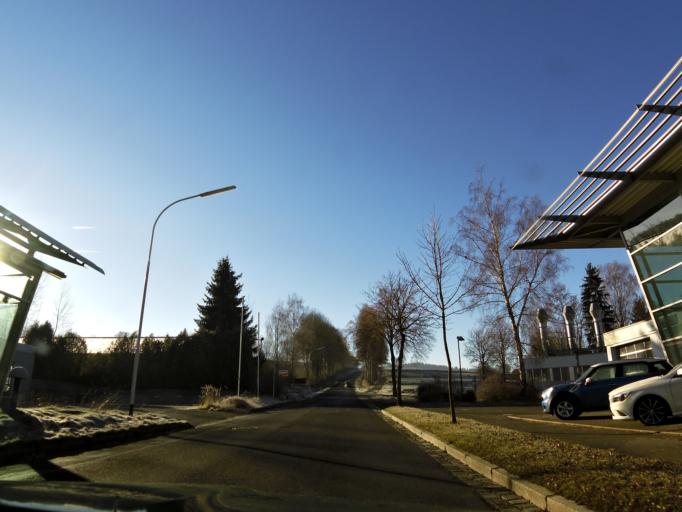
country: DE
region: Bavaria
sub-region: Upper Franconia
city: Wunsiedel
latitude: 50.0303
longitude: 12.0010
